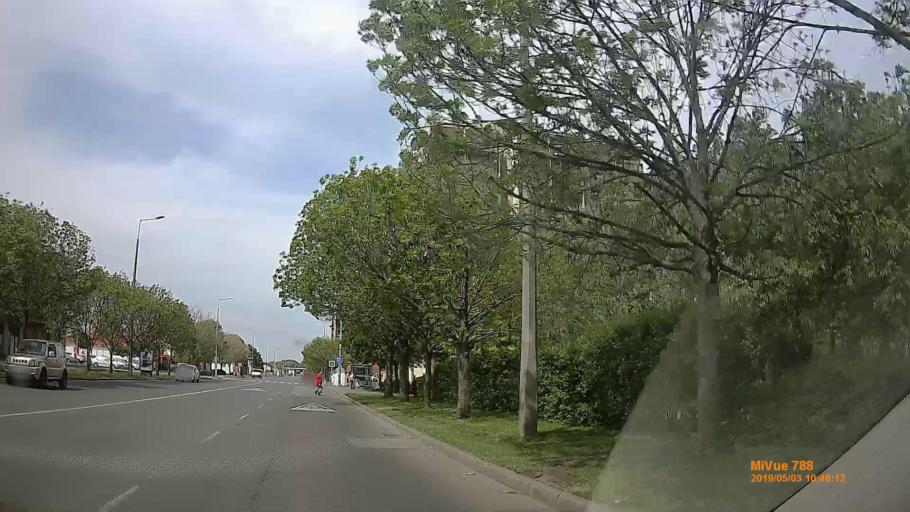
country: HU
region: Jasz-Nagykun-Szolnok
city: Szolnok
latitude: 47.1942
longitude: 20.1822
